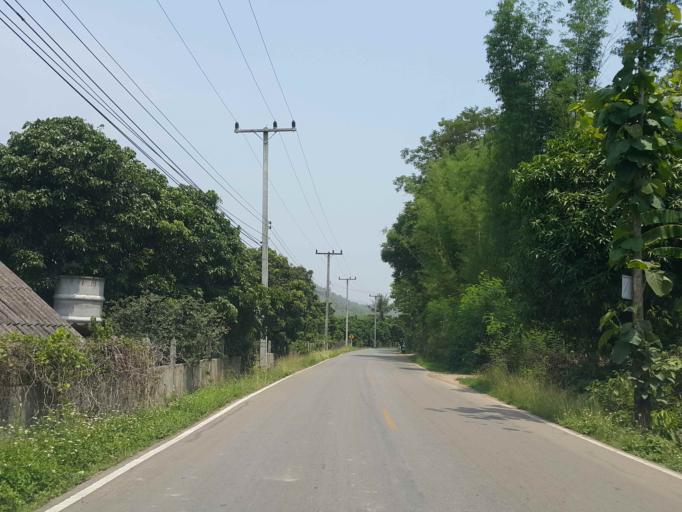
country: TH
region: Chiang Mai
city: Mae Taeng
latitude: 19.0918
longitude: 98.9027
